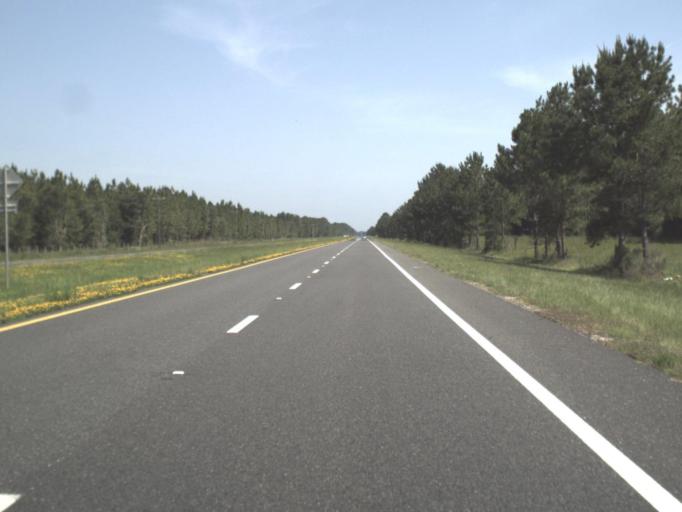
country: US
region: Florida
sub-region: Levy County
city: Chiefland
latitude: 29.4194
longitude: -82.8247
